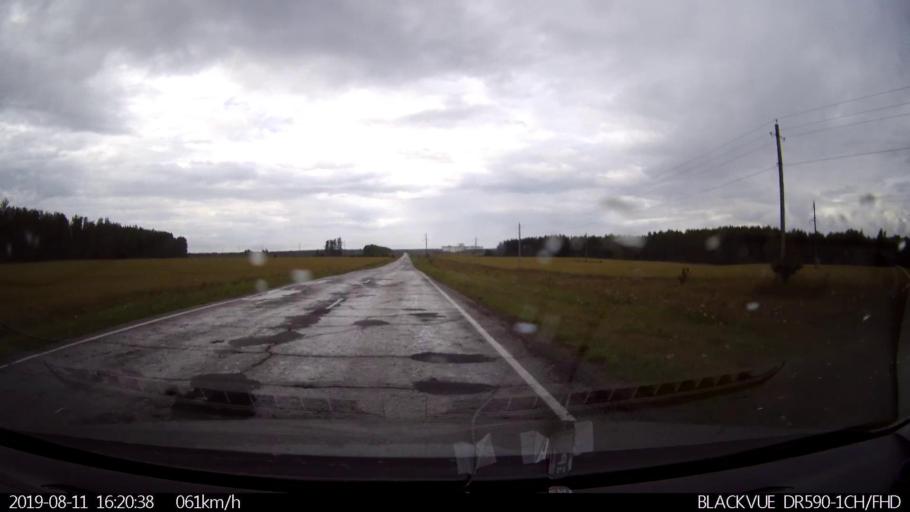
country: RU
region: Ulyanovsk
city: Mayna
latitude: 54.0734
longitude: 47.6019
